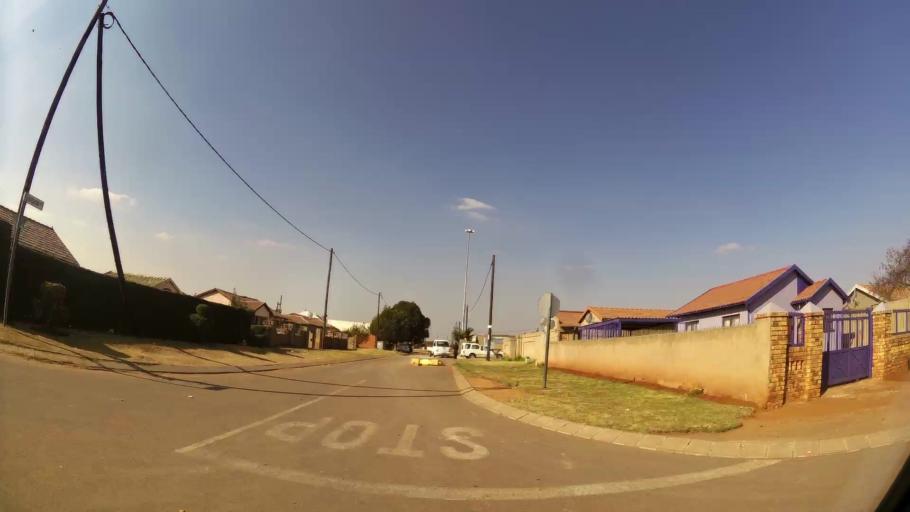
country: ZA
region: Gauteng
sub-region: Ekurhuleni Metropolitan Municipality
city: Benoni
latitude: -26.2263
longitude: 28.3229
